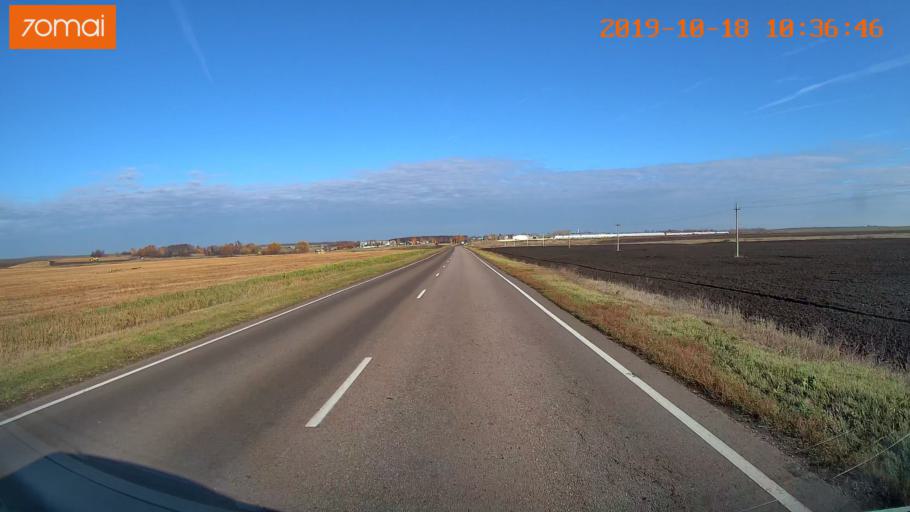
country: RU
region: Tula
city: Kurkino
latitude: 53.5533
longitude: 38.6279
